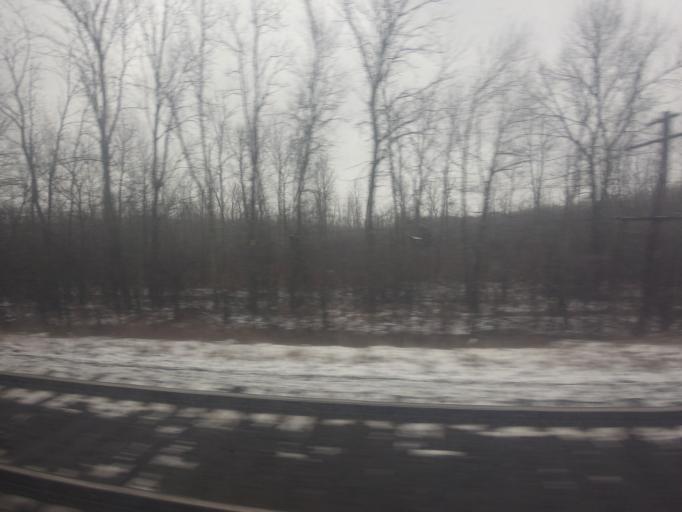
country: CA
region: Ontario
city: Quinte West
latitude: 44.1504
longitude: -77.4806
